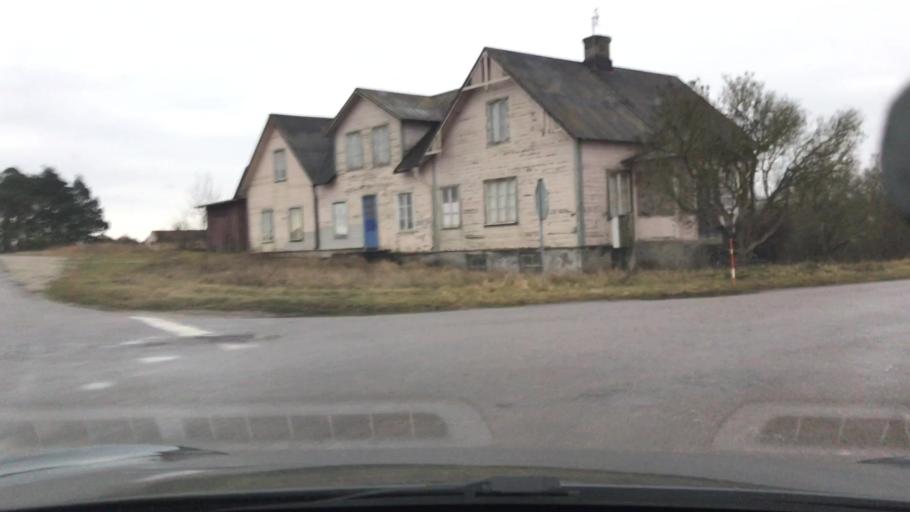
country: SE
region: Gotland
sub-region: Gotland
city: Slite
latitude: 57.3990
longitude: 18.8065
